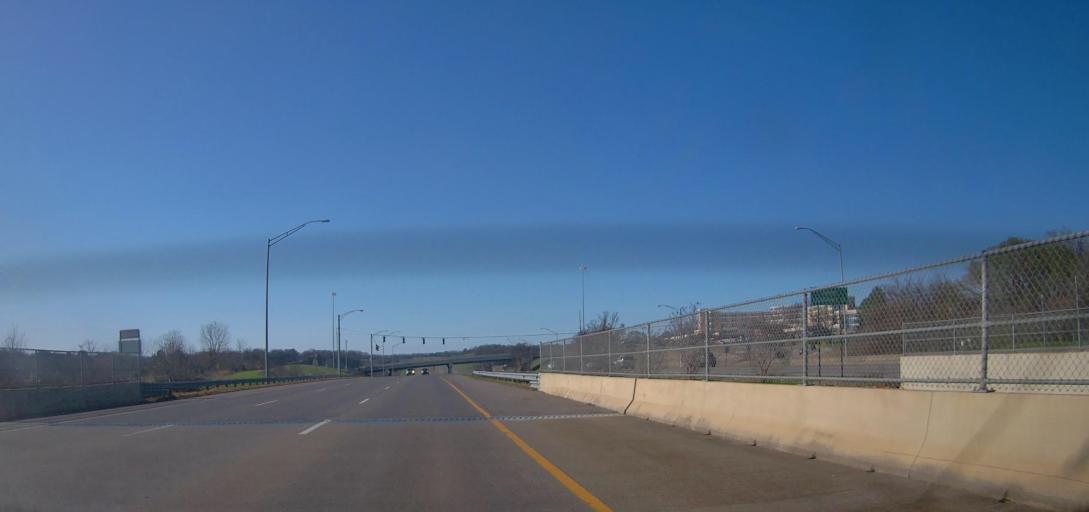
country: US
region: Alabama
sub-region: Lauderdale County
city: East Florence
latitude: 34.8004
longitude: -87.6504
